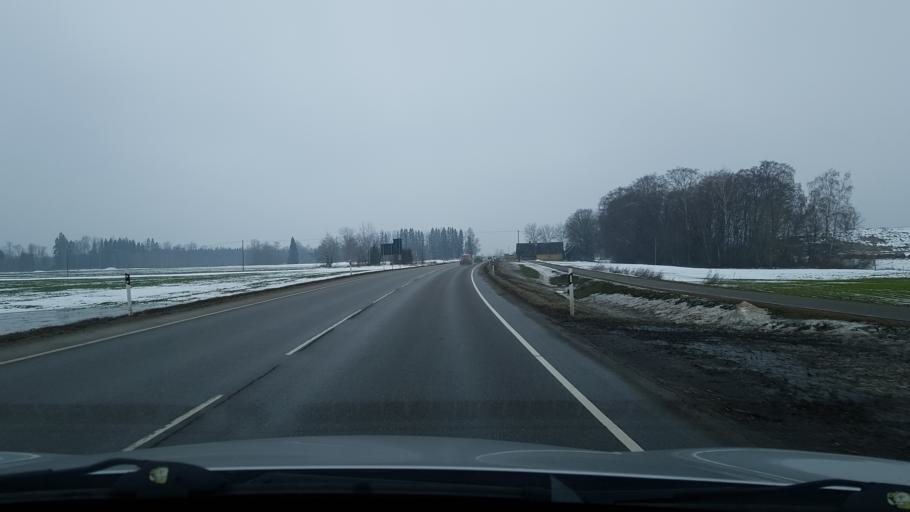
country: EE
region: Viljandimaa
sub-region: Viiratsi vald
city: Viiratsi
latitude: 58.3820
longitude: 25.6706
